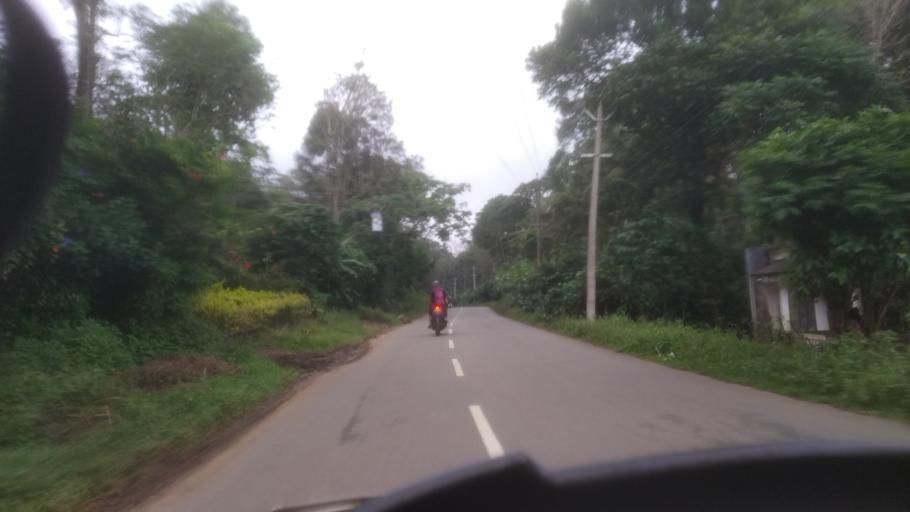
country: IN
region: Tamil Nadu
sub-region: Theni
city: Kombai
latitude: 9.8993
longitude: 77.1848
